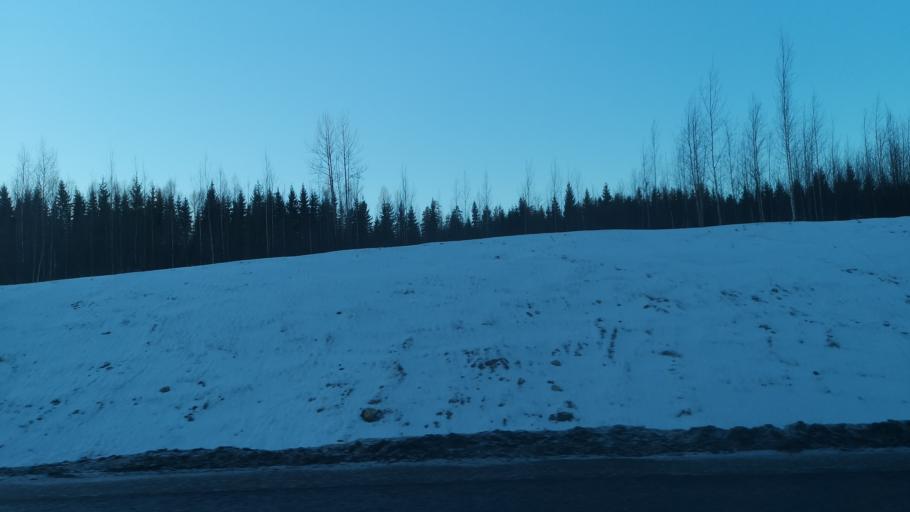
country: FI
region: Southern Savonia
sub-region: Pieksaemaeki
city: Juva
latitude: 61.7823
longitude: 27.5948
